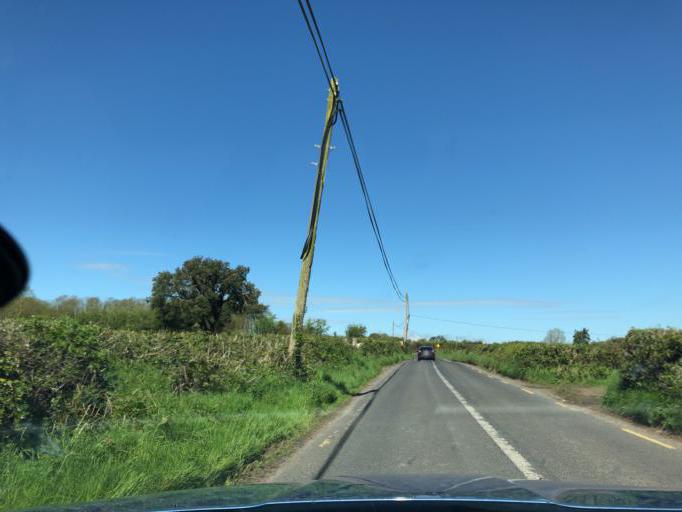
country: IE
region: Connaught
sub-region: County Galway
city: Portumna
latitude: 53.1368
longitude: -8.3634
